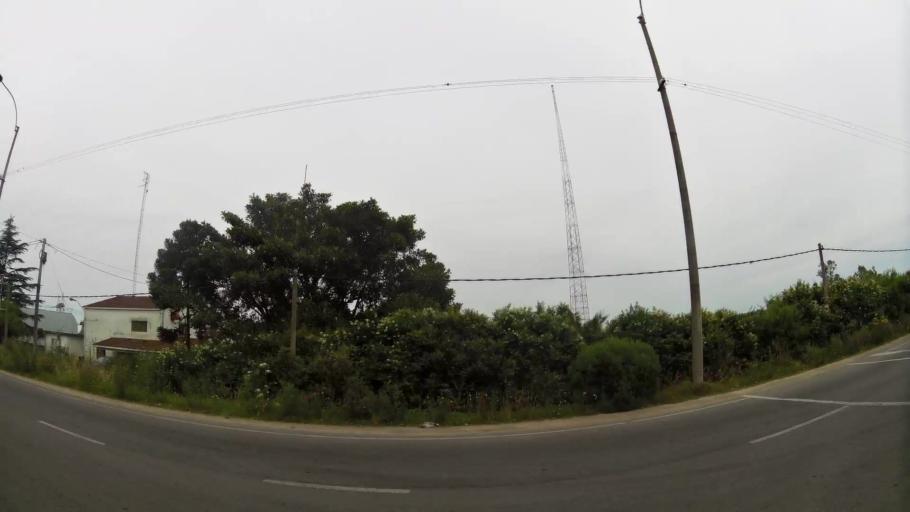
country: UY
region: Canelones
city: La Paz
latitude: -34.7739
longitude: -56.2263
